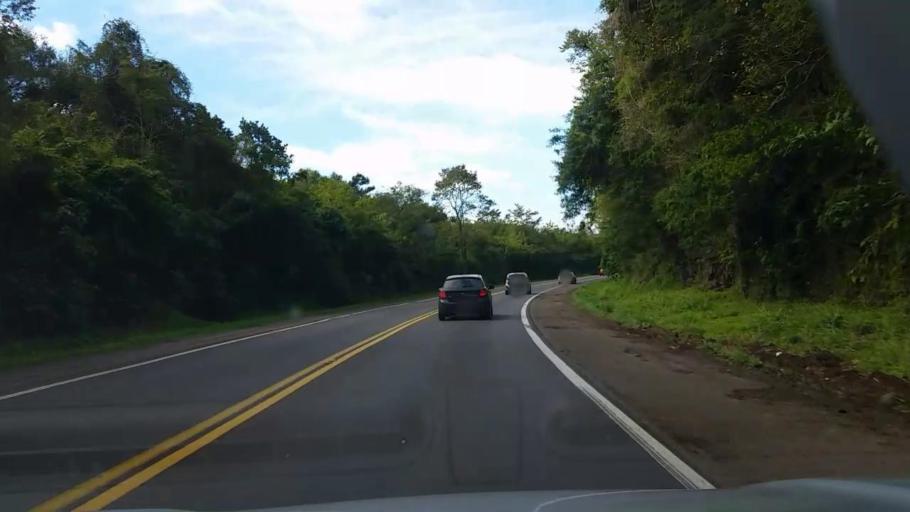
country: BR
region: Rio Grande do Sul
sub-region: Arroio Do Meio
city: Arroio do Meio
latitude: -29.3352
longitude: -52.0906
